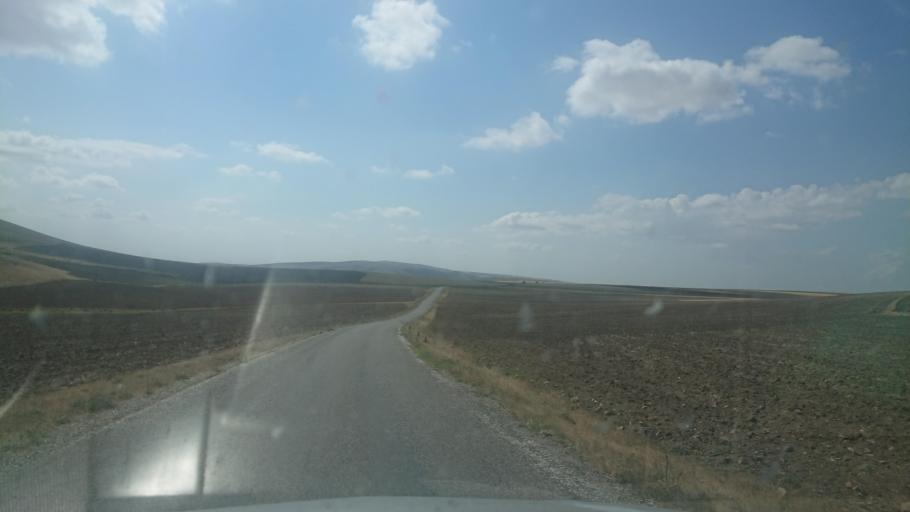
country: TR
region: Aksaray
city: Sariyahsi
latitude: 38.9995
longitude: 33.9764
